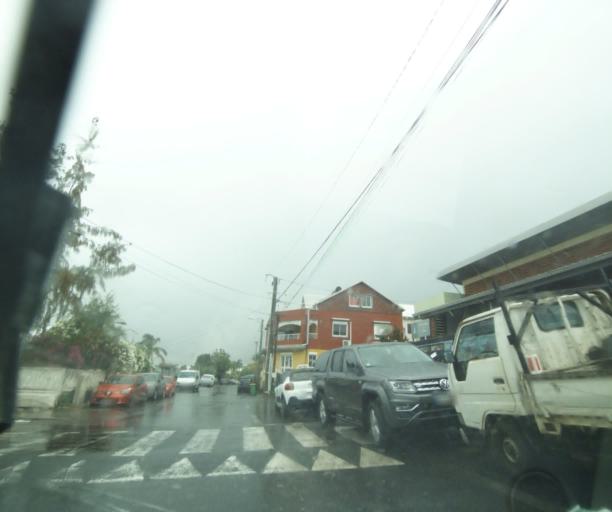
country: RE
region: Reunion
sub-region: Reunion
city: La Possession
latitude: -20.9815
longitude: 55.3273
